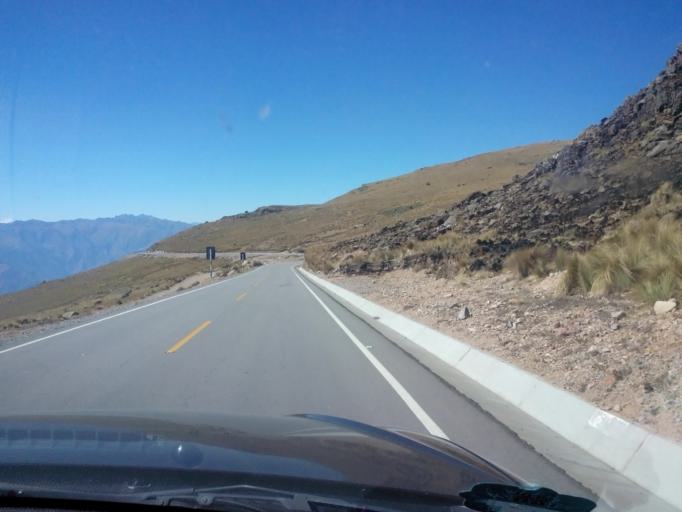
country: PE
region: Ayacucho
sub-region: Provincia de Huamanga
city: Ocros
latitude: -13.3906
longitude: -73.9585
